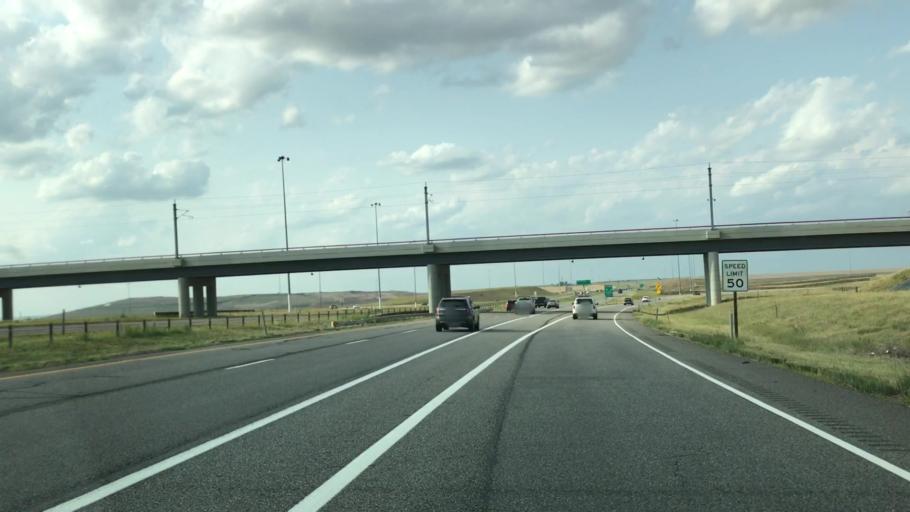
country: US
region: Colorado
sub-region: Adams County
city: Aurora
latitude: 39.8267
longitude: -104.7468
